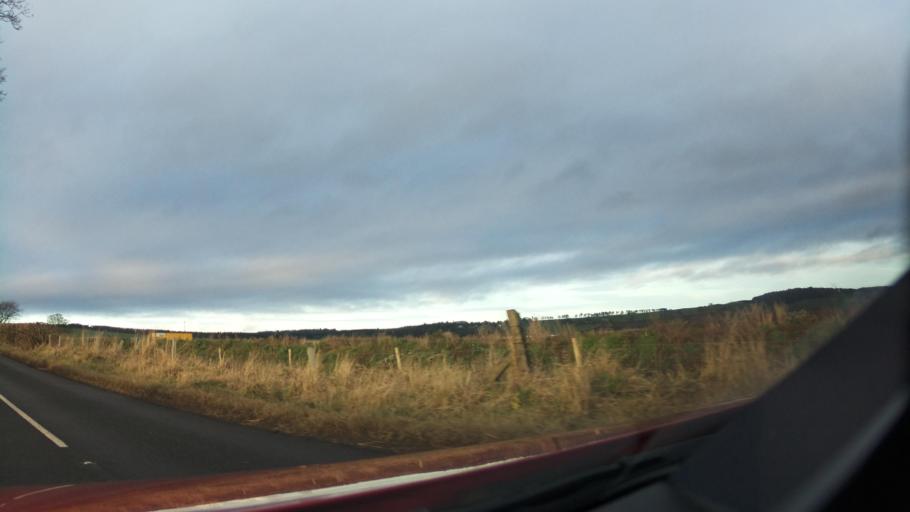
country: GB
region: Scotland
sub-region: Fife
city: Tayport
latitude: 56.5058
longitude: -2.8145
